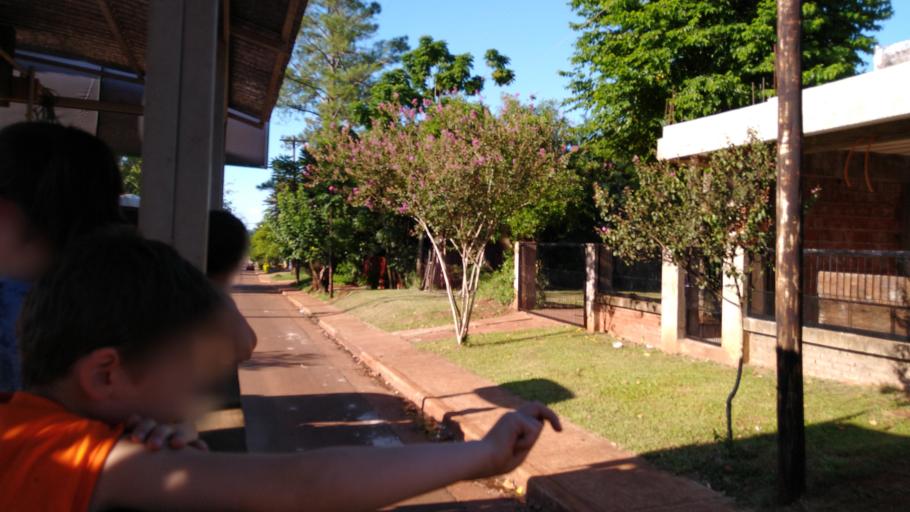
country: AR
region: Misiones
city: Garupa
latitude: -27.4869
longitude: -55.8215
